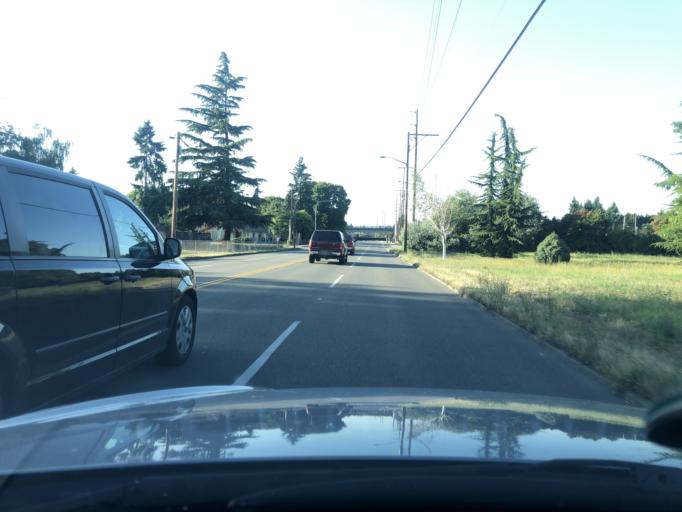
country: US
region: Washington
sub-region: King County
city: Auburn
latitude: 47.3001
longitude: -122.2134
